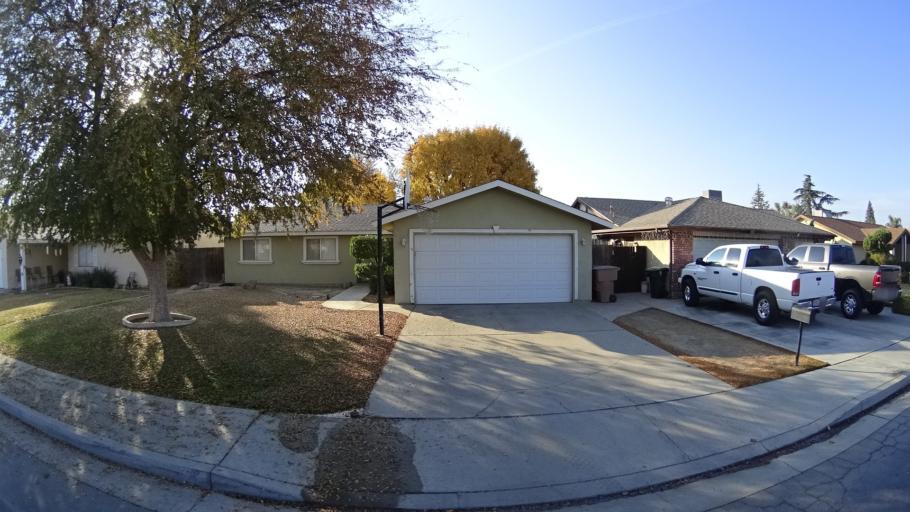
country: US
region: California
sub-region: Kern County
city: Greenfield
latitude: 35.3004
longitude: -119.0221
